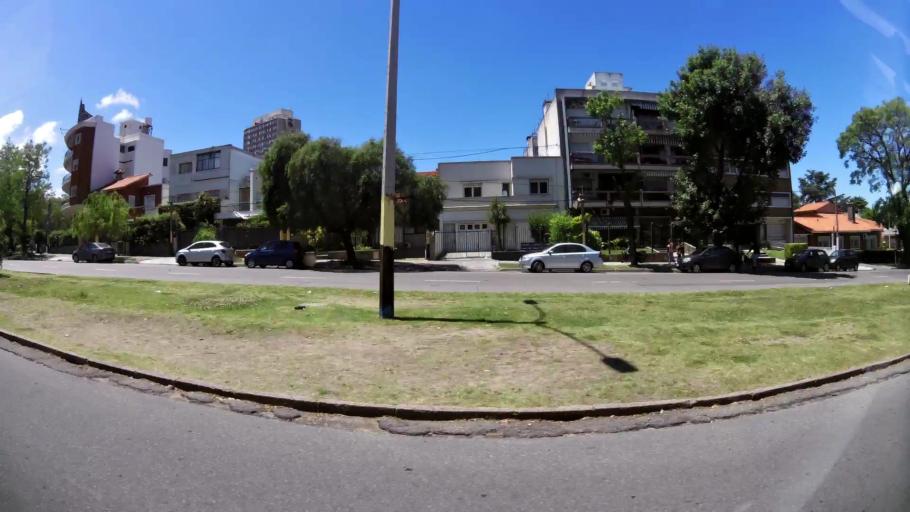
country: UY
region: Montevideo
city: Montevideo
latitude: -34.8948
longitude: -56.1511
